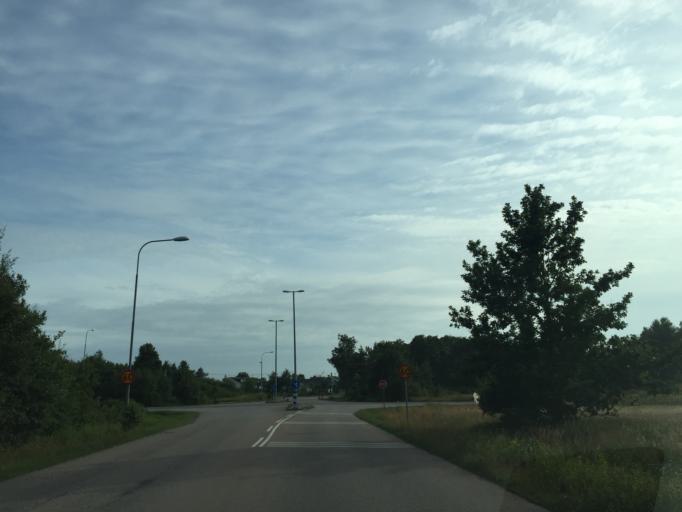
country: SE
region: Halland
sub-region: Falkenbergs Kommun
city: Falkenberg
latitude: 56.8810
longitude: 12.5217
